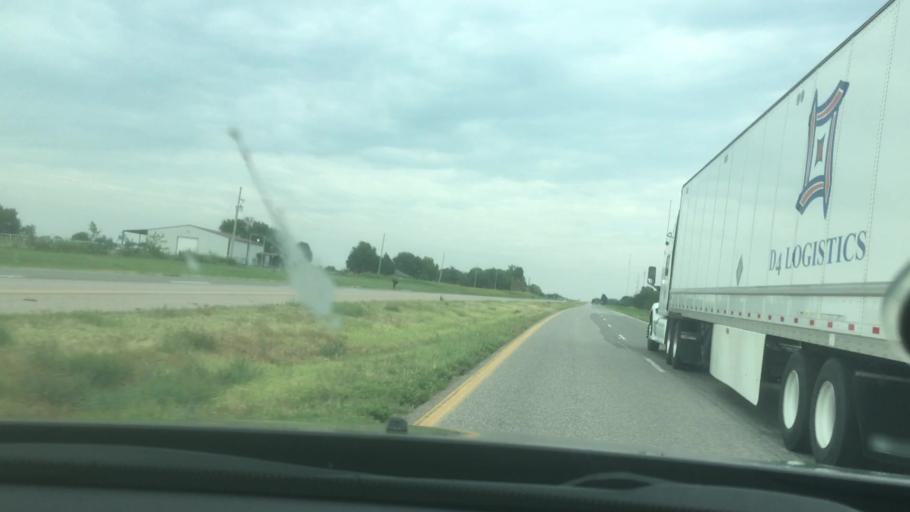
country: US
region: Oklahoma
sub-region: Pontotoc County
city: Ada
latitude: 34.6712
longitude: -96.7804
